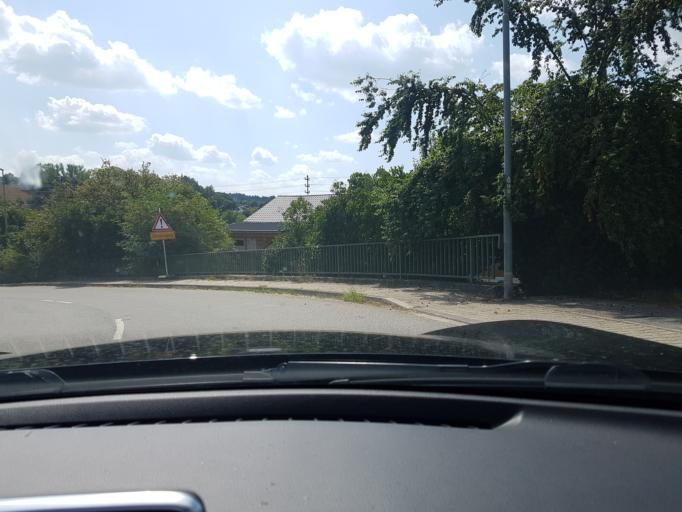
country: DE
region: Baden-Wuerttemberg
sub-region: Karlsruhe Region
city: Limbach
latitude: 49.4253
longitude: 9.2372
